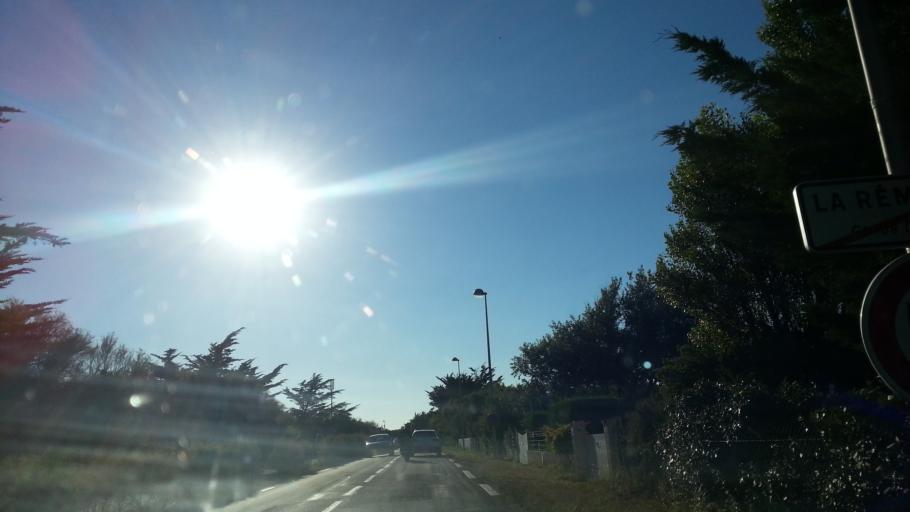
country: FR
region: Poitou-Charentes
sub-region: Departement de la Charente-Maritime
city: Dolus-d'Oleron
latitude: 45.9009
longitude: -1.2925
